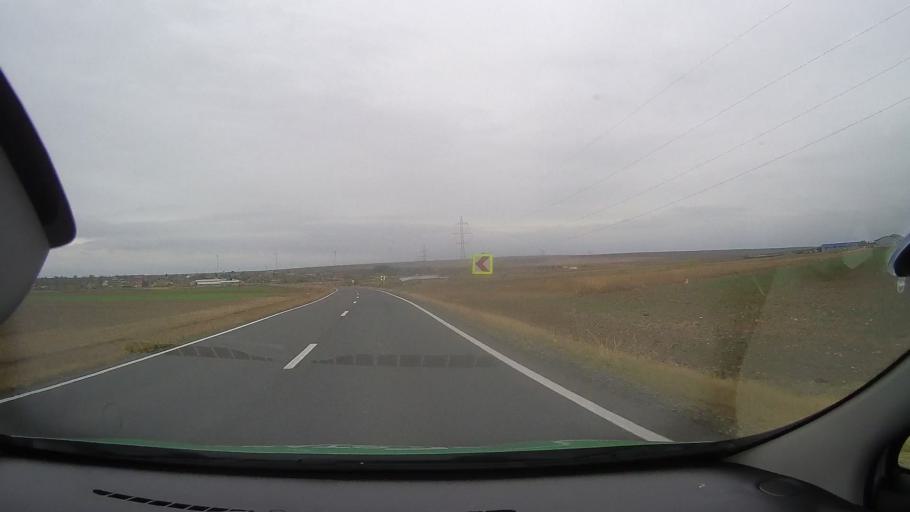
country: RO
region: Constanta
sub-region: Comuna Nicolae Balcescu
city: Dorobantu
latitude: 44.4160
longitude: 28.3157
